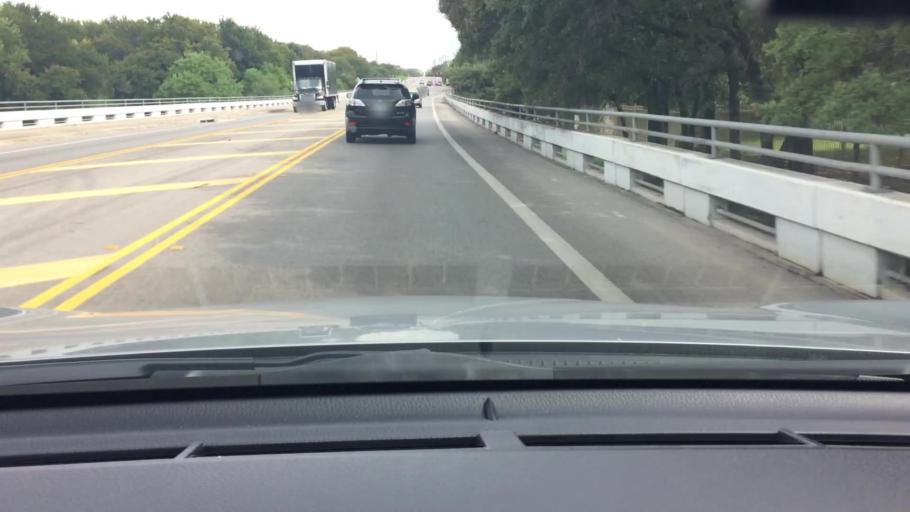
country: US
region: Texas
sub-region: Bexar County
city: Shavano Park
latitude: 29.5537
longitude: -98.5445
